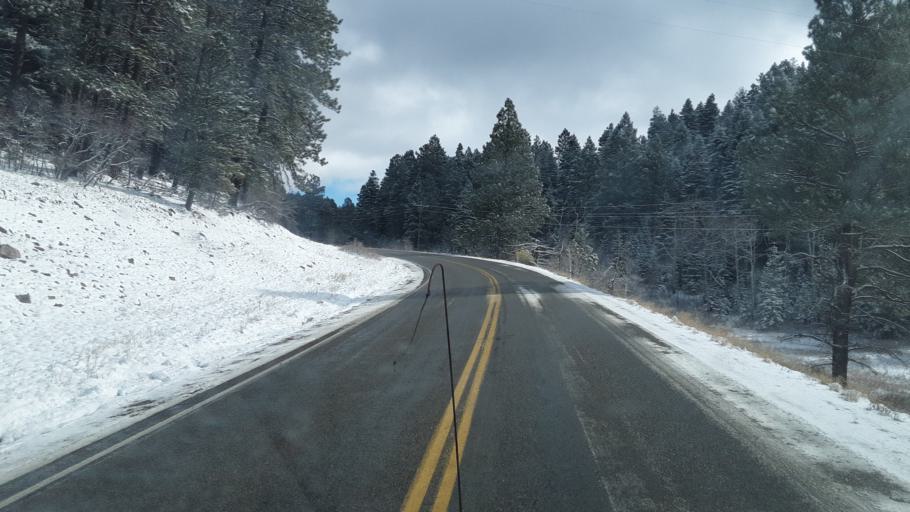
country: US
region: Colorado
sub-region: La Plata County
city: Bayfield
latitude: 37.3578
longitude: -107.6673
